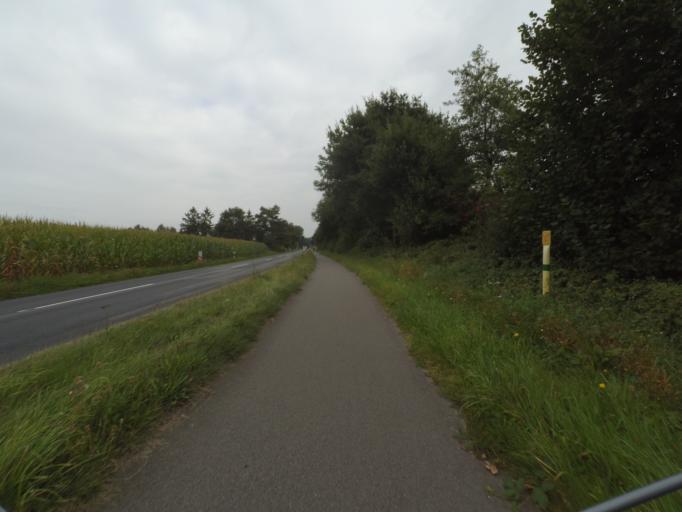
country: NL
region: Overijssel
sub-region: Gemeente Losser
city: Losser
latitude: 52.2835
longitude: 7.0839
